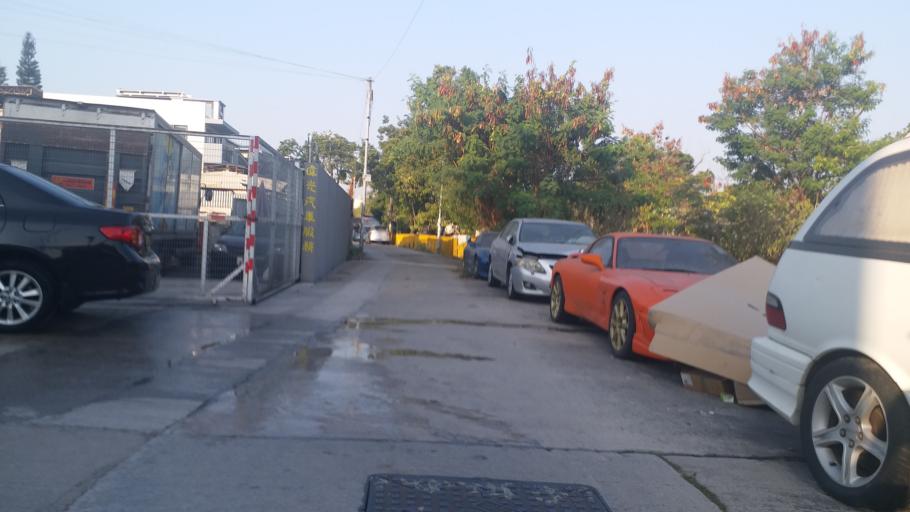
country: HK
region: Tuen Mun
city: Tuen Mun
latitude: 22.4197
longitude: 113.9811
